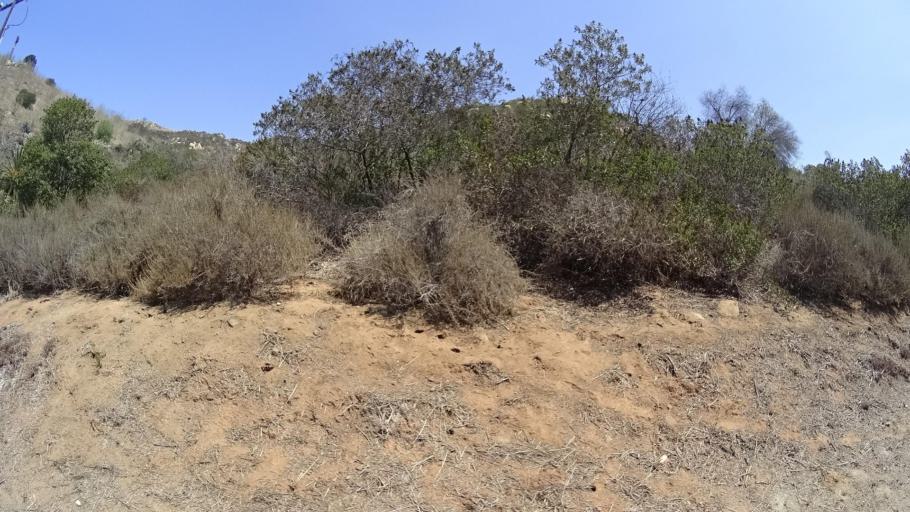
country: US
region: California
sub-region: San Diego County
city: Bonsall
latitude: 33.2673
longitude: -117.2096
